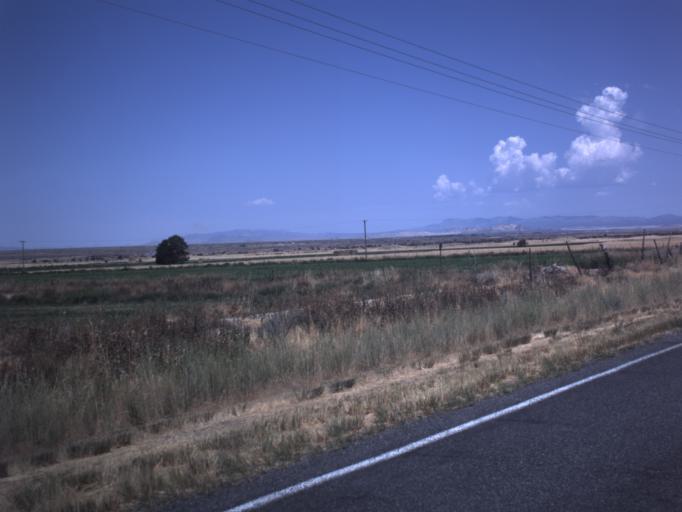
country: US
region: Utah
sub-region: Millard County
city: Delta
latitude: 39.4091
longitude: -112.3321
